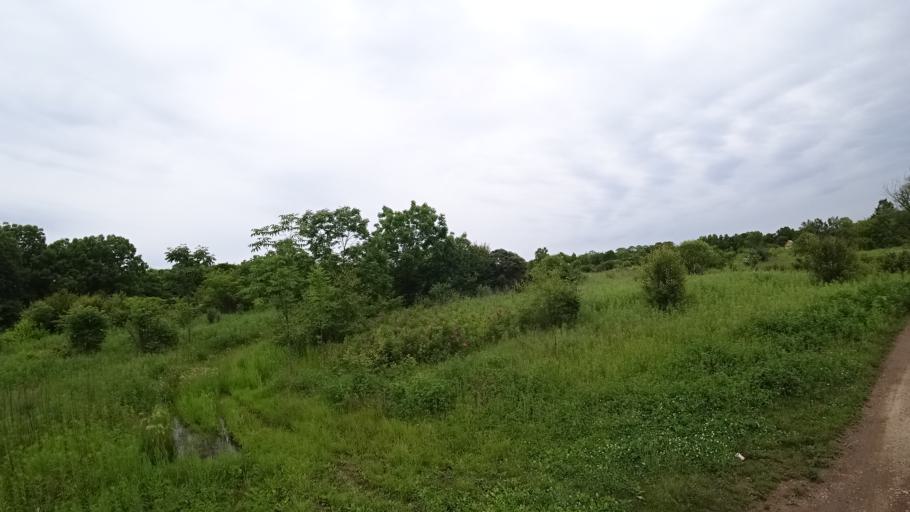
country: RU
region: Primorskiy
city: Novosysoyevka
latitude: 44.2112
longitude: 133.3266
